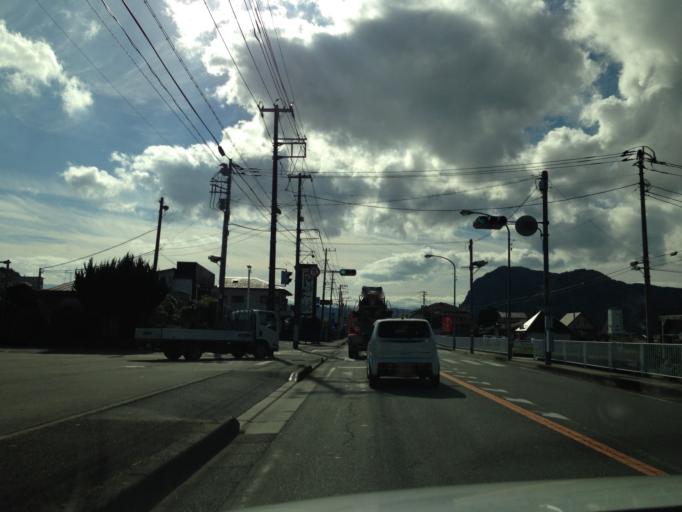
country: JP
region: Shizuoka
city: Mishima
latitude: 35.0267
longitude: 138.9480
